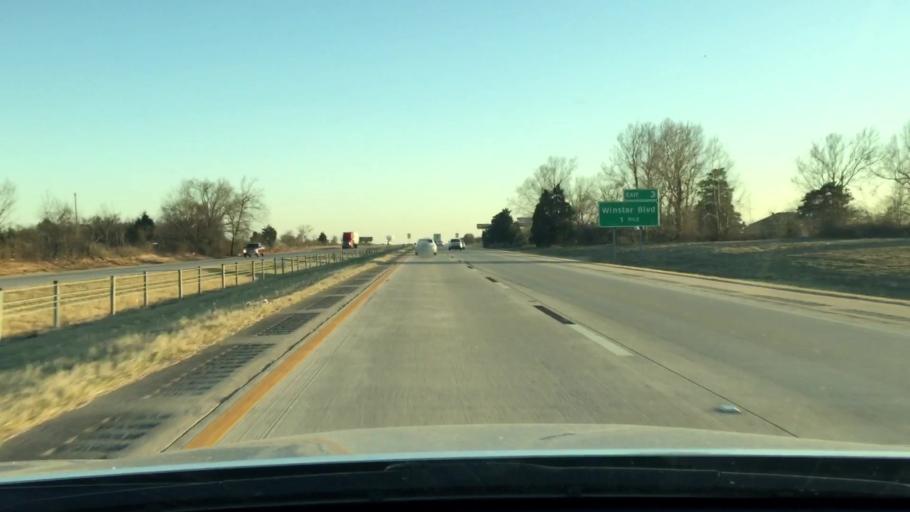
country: US
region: Oklahoma
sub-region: Love County
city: Marietta
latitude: 33.7890
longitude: -97.1350
